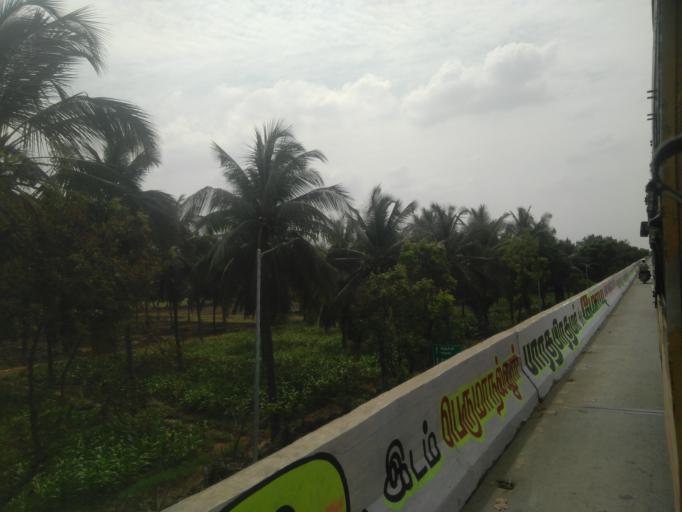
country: IN
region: Tamil Nadu
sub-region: Coimbatore
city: Irugur
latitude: 11.0022
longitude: 77.0581
